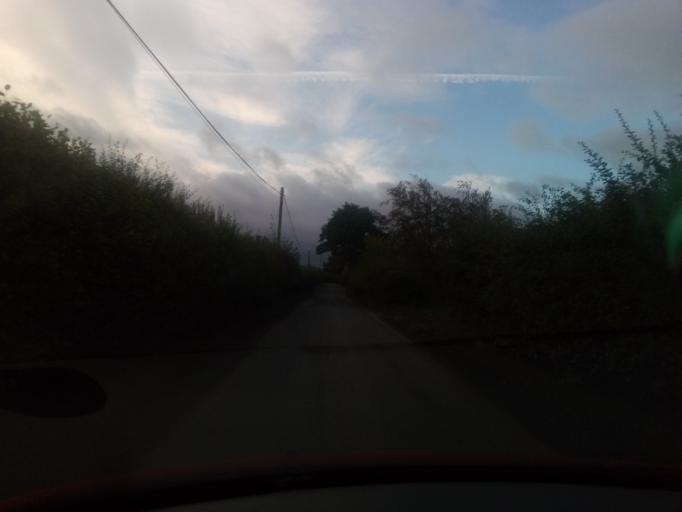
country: GB
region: Scotland
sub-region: The Scottish Borders
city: Jedburgh
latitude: 55.3824
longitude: -2.6432
